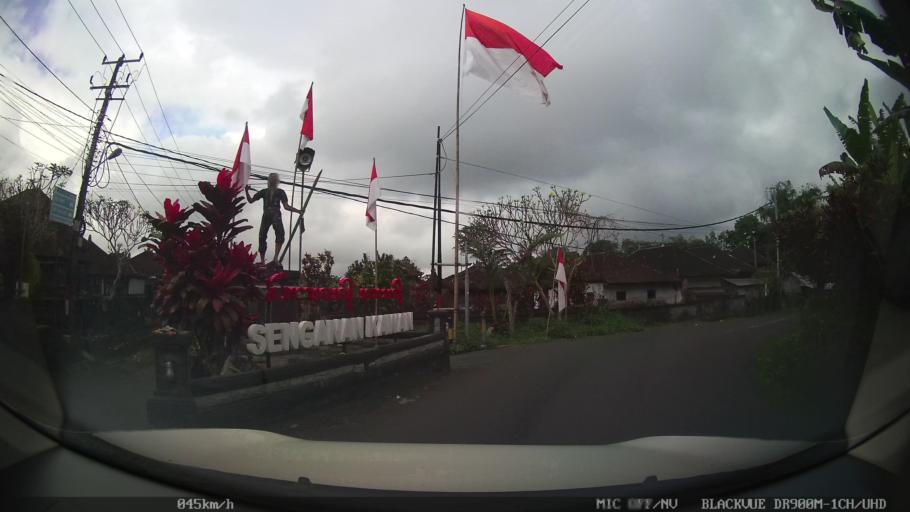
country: ID
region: Bali
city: Empalan
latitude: -8.3745
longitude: 115.1568
